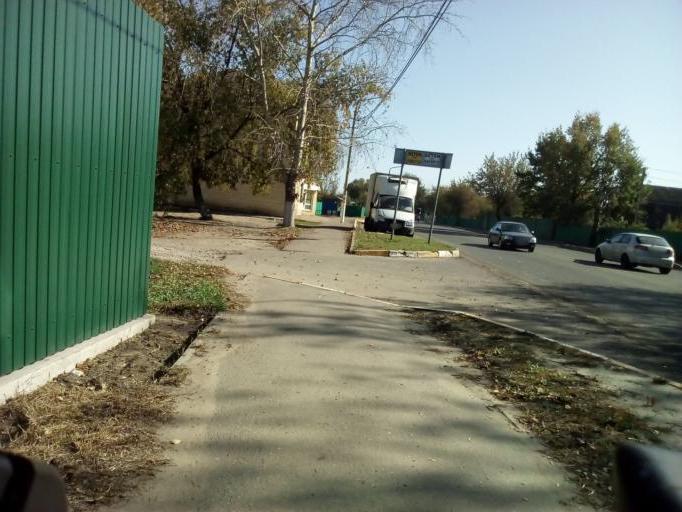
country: RU
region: Moskovskaya
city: Ramenskoye
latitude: 55.5572
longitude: 38.2605
